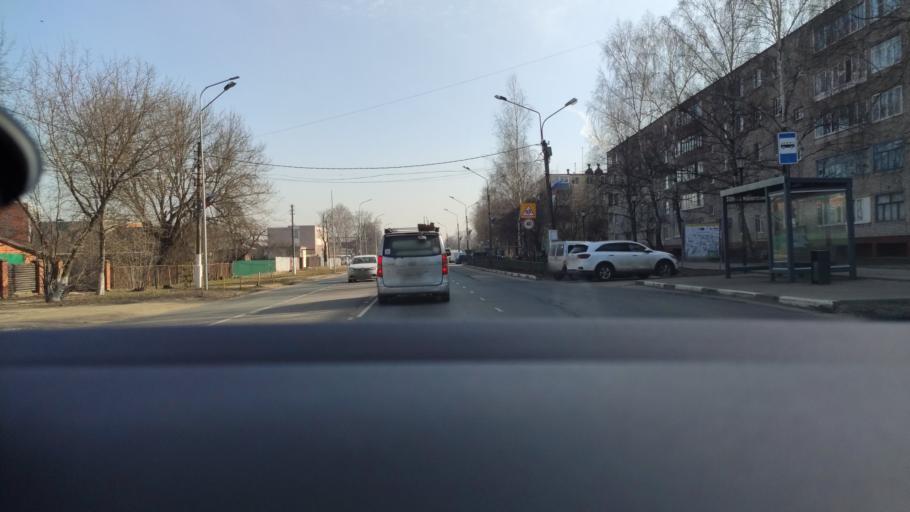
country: RU
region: Moskovskaya
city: Staraya Kupavna
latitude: 55.8107
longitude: 38.1764
